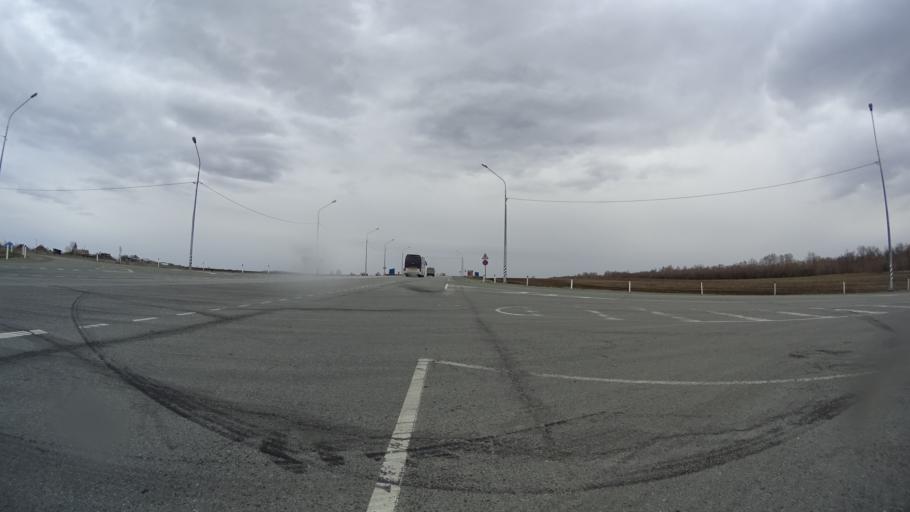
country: RU
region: Chelyabinsk
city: Krasnogorskiy
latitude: 54.6737
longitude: 61.2492
